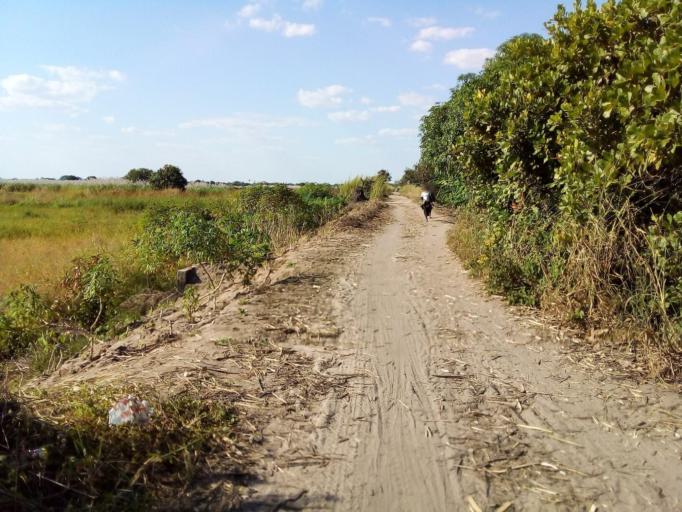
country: MZ
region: Zambezia
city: Quelimane
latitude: -17.5864
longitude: 36.8402
